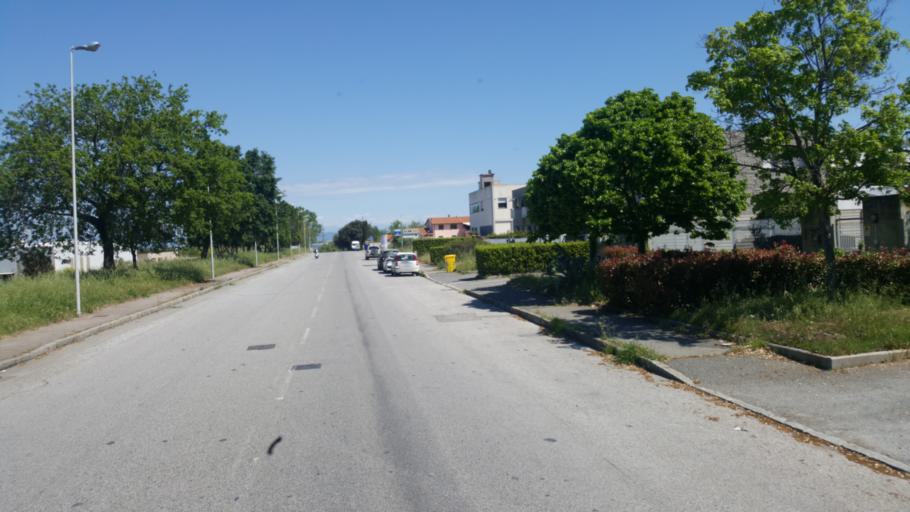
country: IT
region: Tuscany
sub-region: Provincia di Livorno
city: Livorno
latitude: 43.5725
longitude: 10.3433
